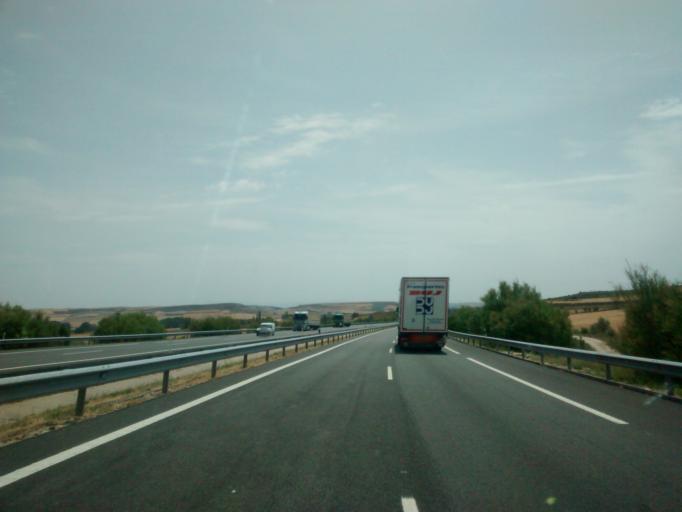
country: ES
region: Castille and Leon
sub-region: Provincia de Burgos
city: Rabe de las Calzadas
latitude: 42.3698
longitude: -3.8517
